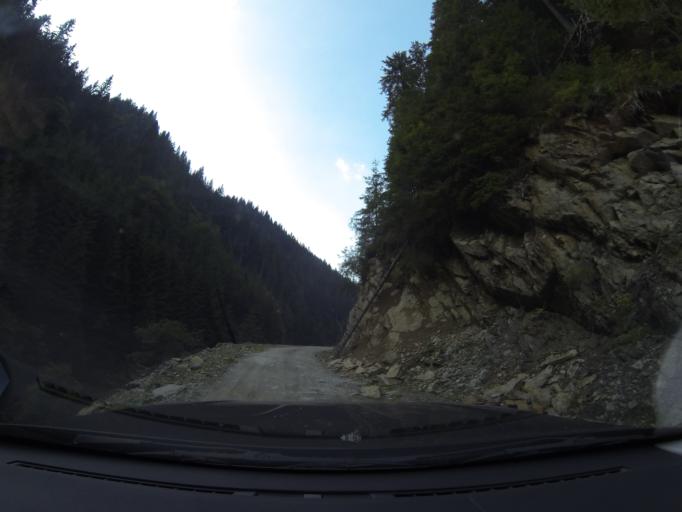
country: RO
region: Brasov
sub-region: Oras Victoria
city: Victoria
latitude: 45.5395
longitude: 24.6781
